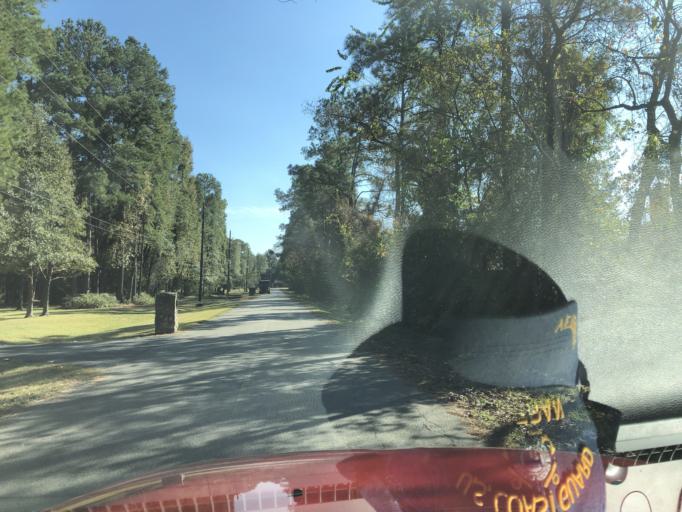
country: US
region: Texas
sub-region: Harris County
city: Tomball
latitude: 30.0322
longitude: -95.5431
